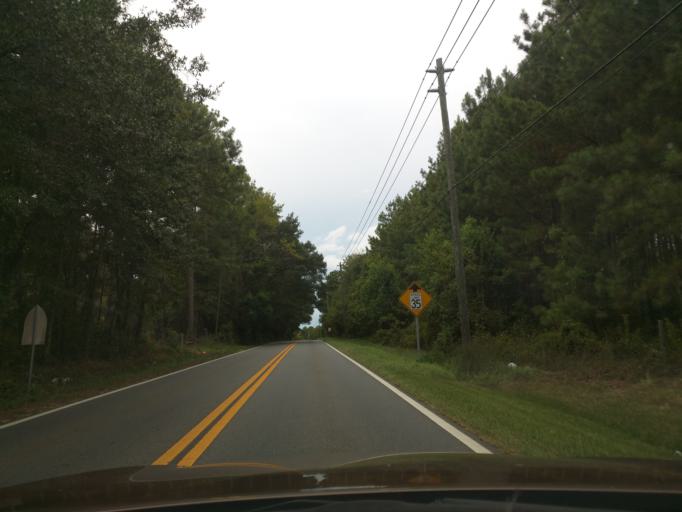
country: US
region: Florida
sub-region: Leon County
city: Tallahassee
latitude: 30.5853
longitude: -84.2484
